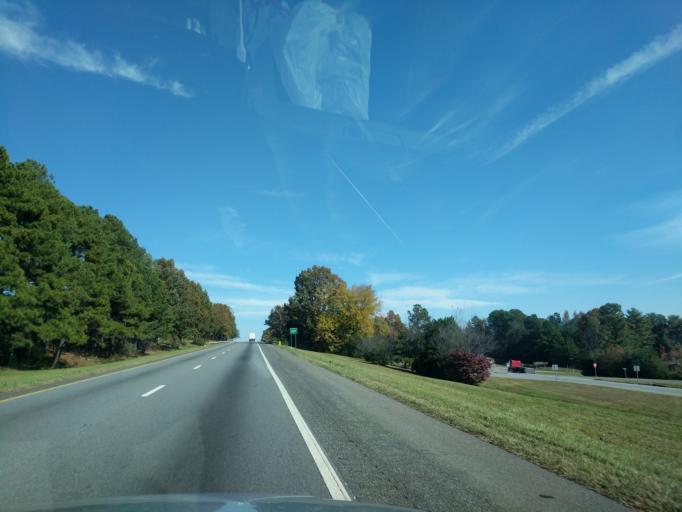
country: US
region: North Carolina
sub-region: Cleveland County
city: White Plains
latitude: 35.1767
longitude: -81.4167
